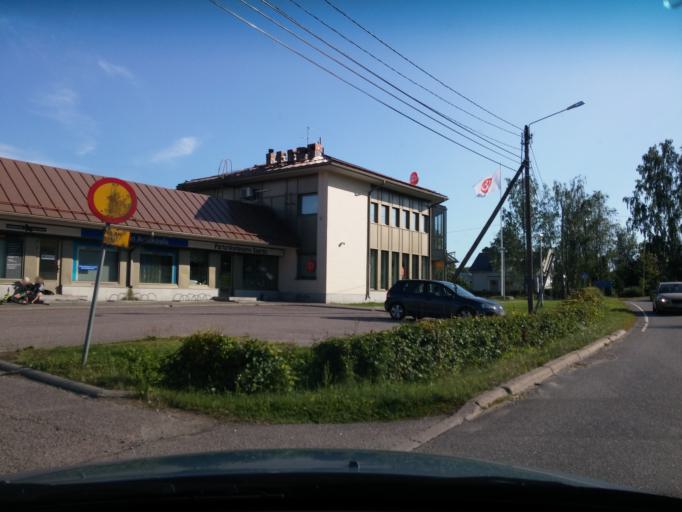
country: FI
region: Uusimaa
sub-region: Porvoo
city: Askola
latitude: 60.4937
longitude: 25.5407
